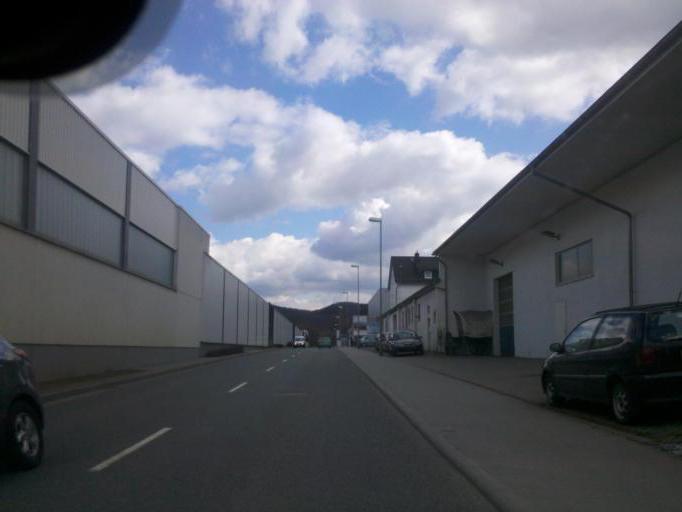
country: DE
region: Hesse
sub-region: Regierungsbezirk Giessen
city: Haiger
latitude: 50.7439
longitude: 8.2170
